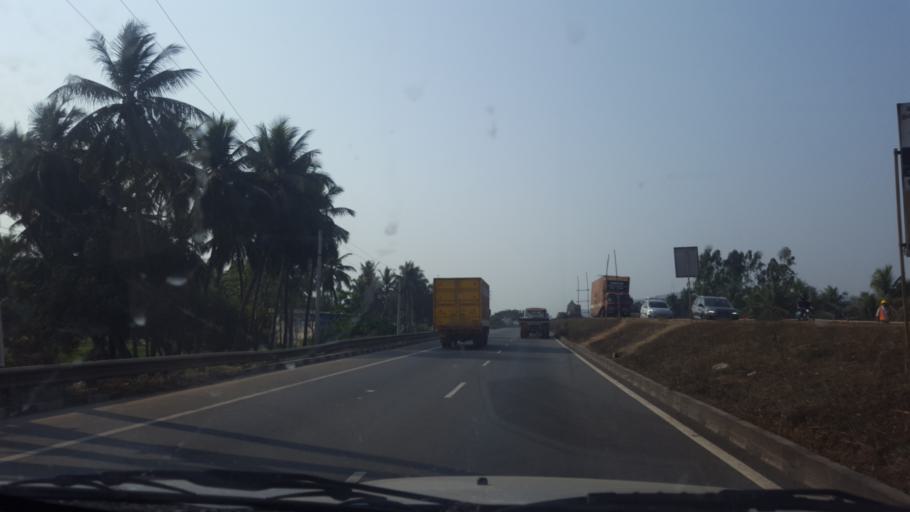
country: IN
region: Andhra Pradesh
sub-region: Vishakhapatnam
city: Anakapalle
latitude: 17.6771
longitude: 82.9948
